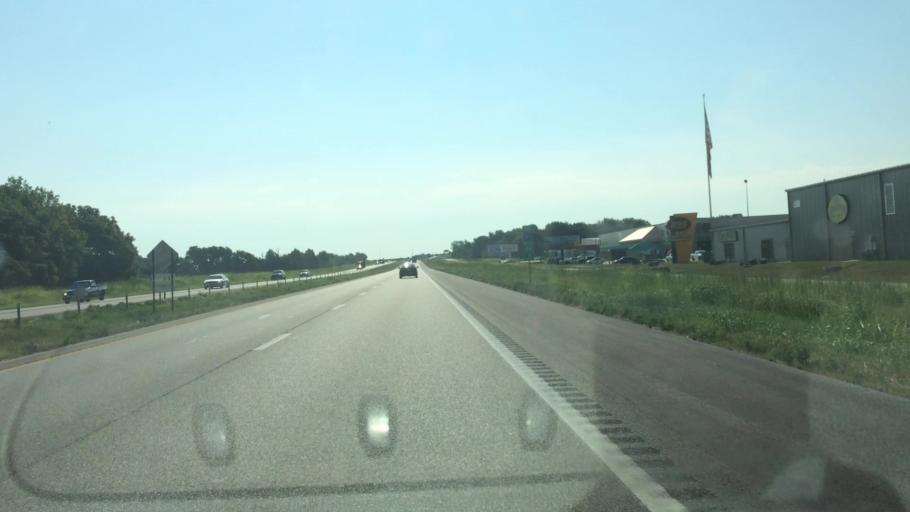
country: US
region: Missouri
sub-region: Greene County
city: Strafford
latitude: 37.2501
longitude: -93.1979
